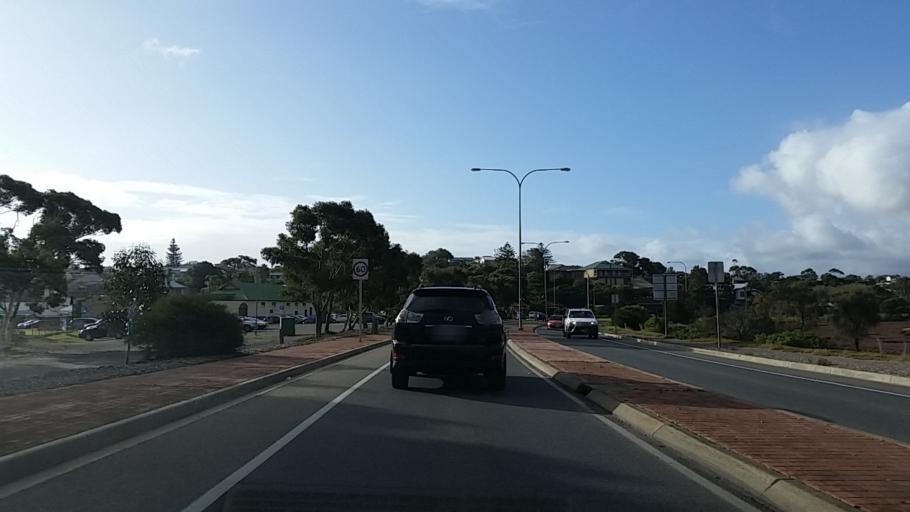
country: AU
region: South Australia
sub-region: Adelaide
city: Port Noarlunga
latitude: -35.1504
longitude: 138.4724
